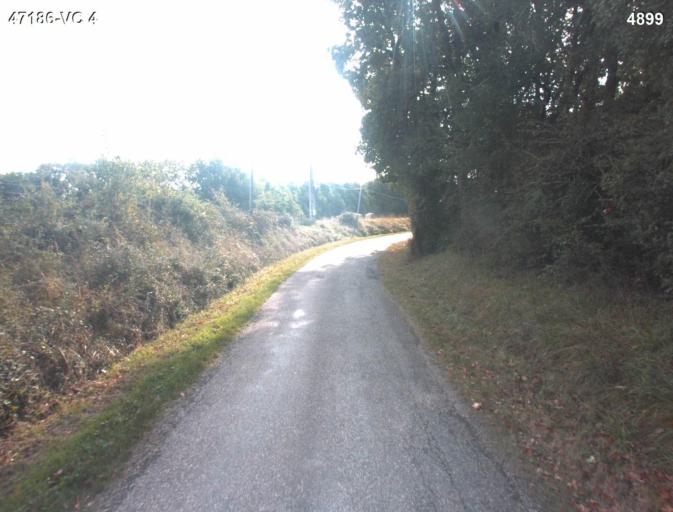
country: FR
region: Aquitaine
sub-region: Departement du Lot-et-Garonne
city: Sainte-Colombe-en-Bruilhois
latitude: 44.1915
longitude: 0.4562
